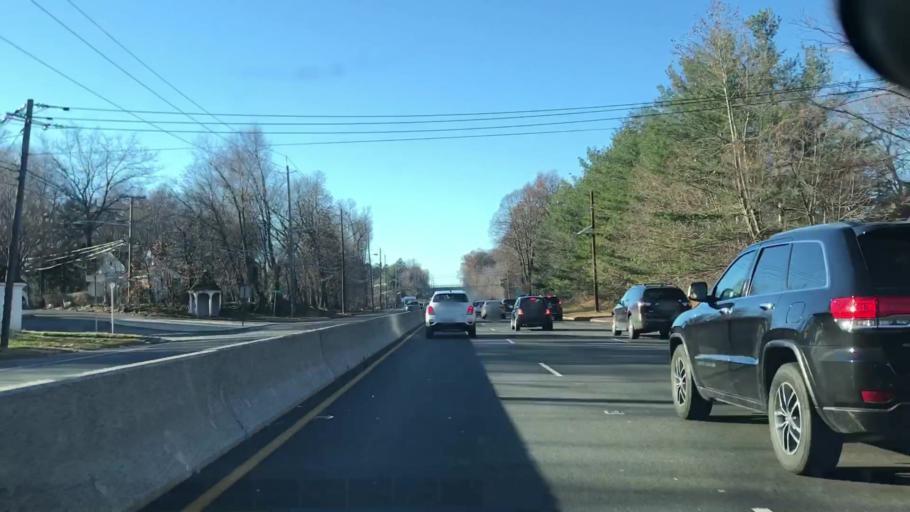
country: US
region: New Jersey
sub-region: Bergen County
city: Teaneck
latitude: 40.8897
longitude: -74.0007
